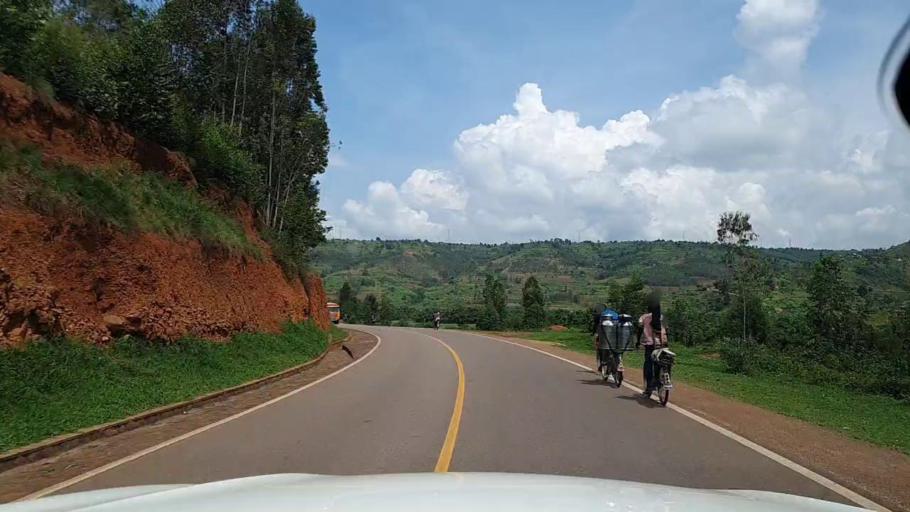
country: RW
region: Kigali
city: Kigali
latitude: -1.8500
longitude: 30.0969
